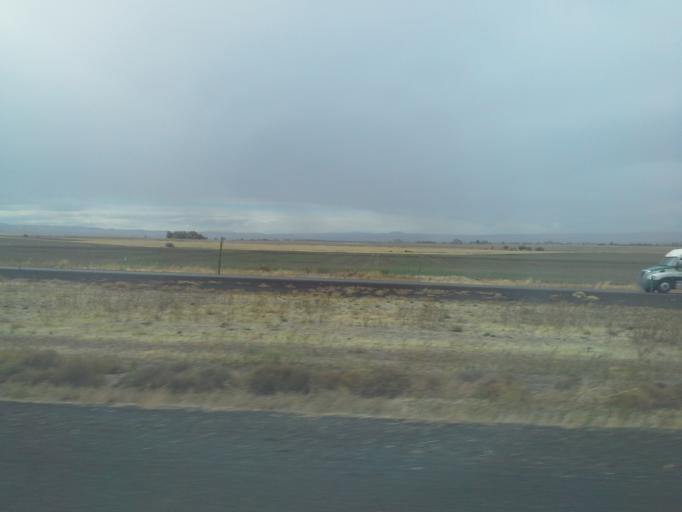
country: US
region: Oregon
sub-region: Umatilla County
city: Mission
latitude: 45.6192
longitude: -118.6543
